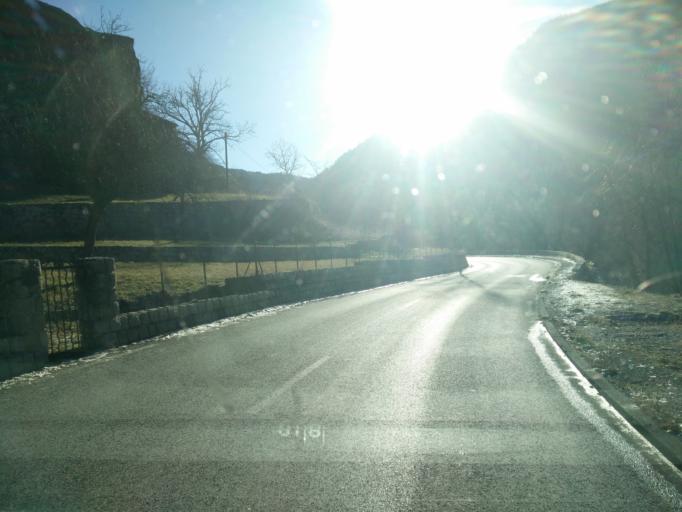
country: FR
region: Provence-Alpes-Cote d'Azur
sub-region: Departement des Alpes-de-Haute-Provence
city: Annot
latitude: 43.9591
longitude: 6.6753
